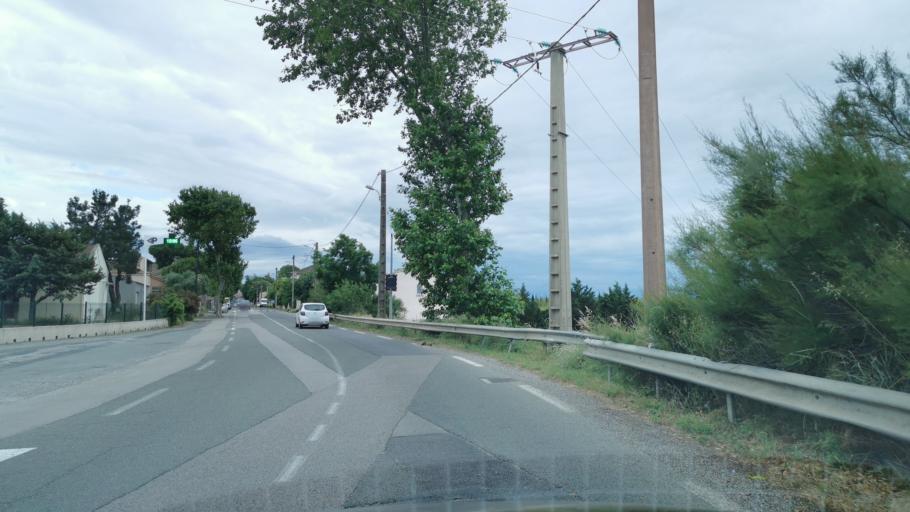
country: FR
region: Languedoc-Roussillon
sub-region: Departement de l'Aude
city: Marcorignan
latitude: 43.2305
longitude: 2.9239
